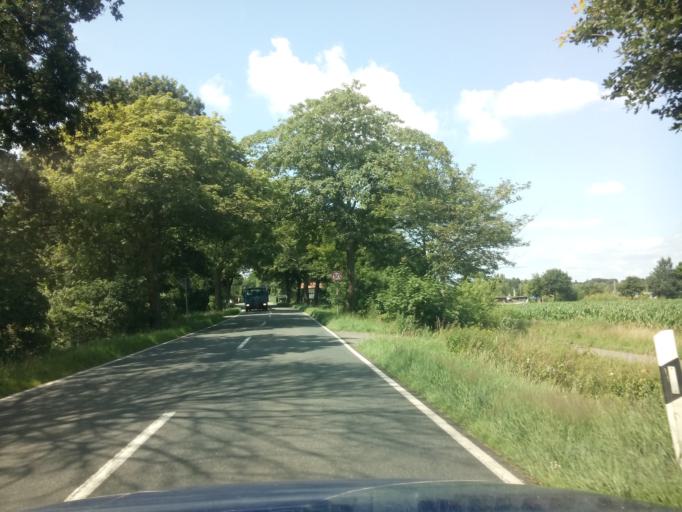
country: DE
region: Lower Saxony
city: Worpswede
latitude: 53.2639
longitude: 8.9187
